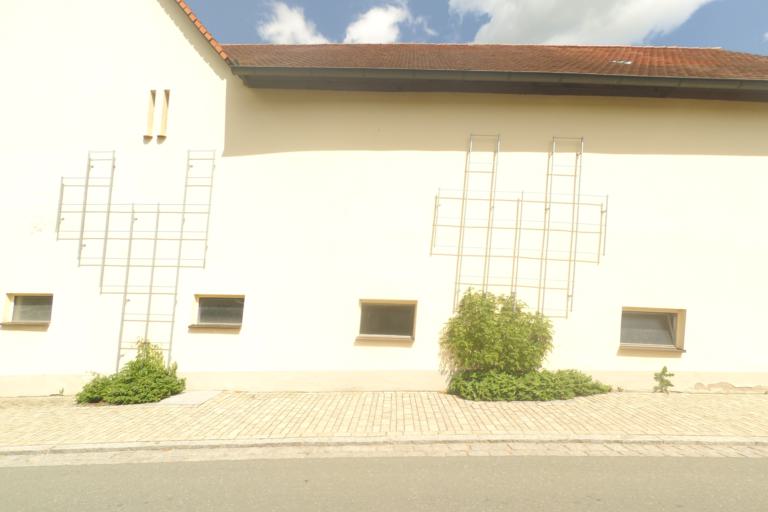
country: DE
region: Bavaria
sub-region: Upper Franconia
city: Hallerndorf
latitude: 49.7852
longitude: 10.9566
